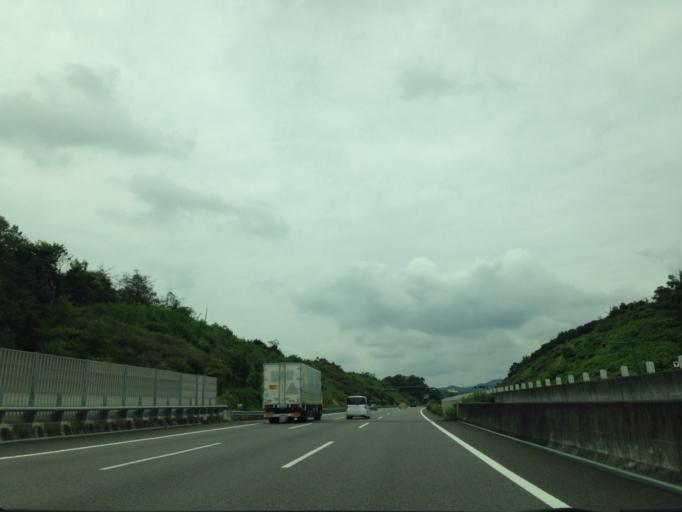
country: JP
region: Shizuoka
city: Hamakita
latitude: 34.8375
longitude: 137.7722
